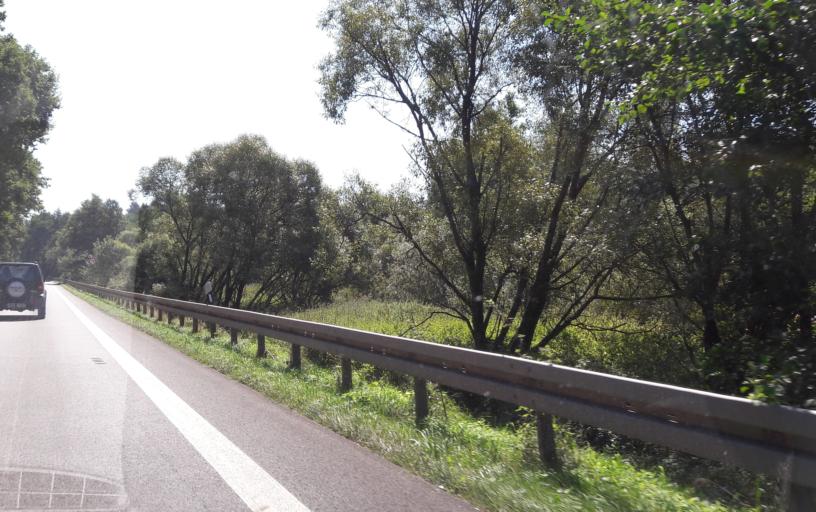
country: DE
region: Saarland
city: Nohfelden
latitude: 49.5841
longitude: 7.1274
